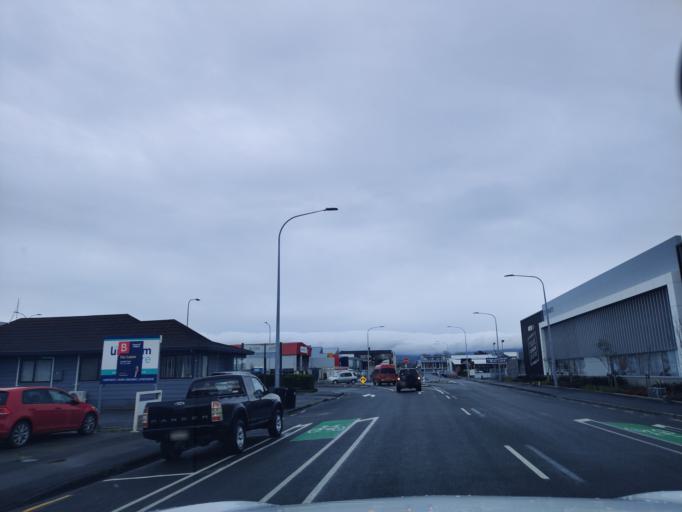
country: NZ
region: Manawatu-Wanganui
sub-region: Palmerston North City
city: Palmerston North
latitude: -40.3546
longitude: 175.6036
